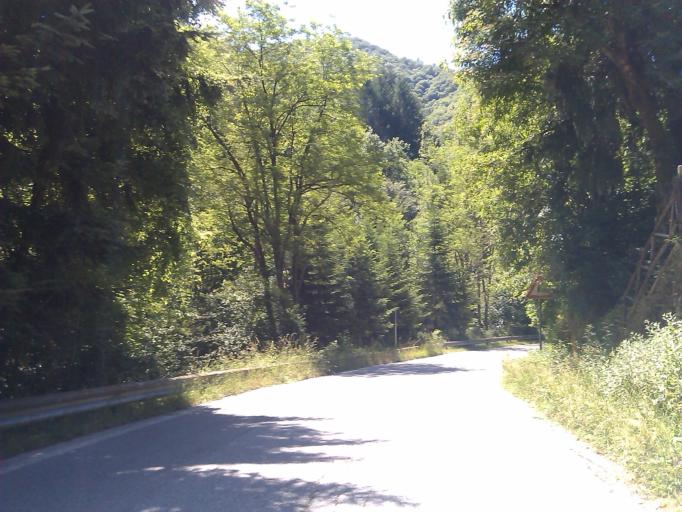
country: IT
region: Tuscany
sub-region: Provincia di Prato
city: Cantagallo
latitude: 44.0528
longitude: 11.0457
